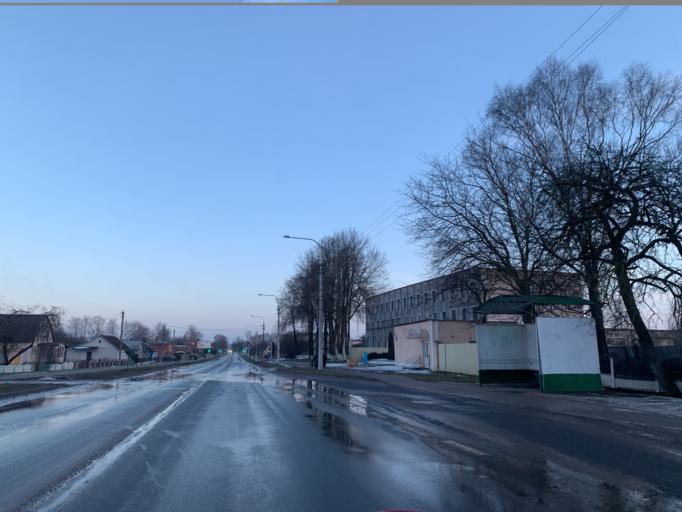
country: BY
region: Minsk
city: Nyasvizh
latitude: 53.2284
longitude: 26.6628
